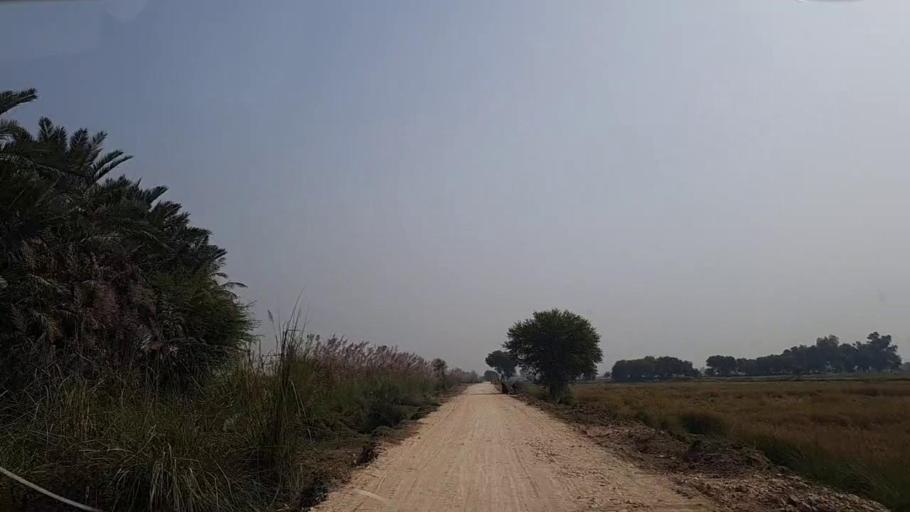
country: PK
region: Sindh
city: Garhi Yasin
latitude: 27.9221
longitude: 68.5722
